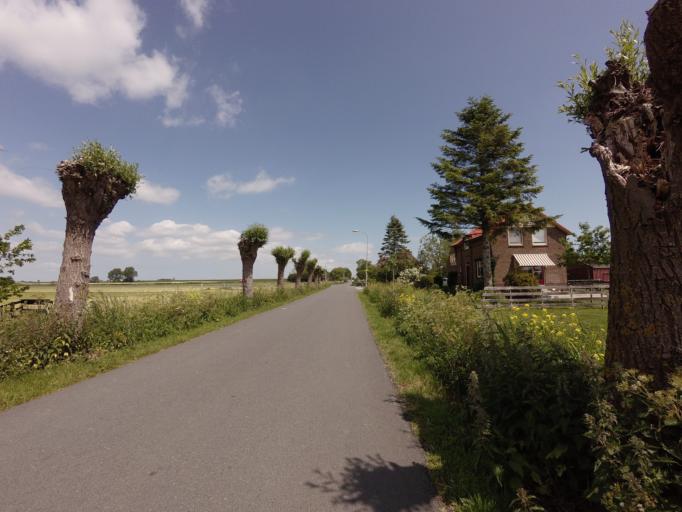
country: NL
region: North Holland
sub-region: Gemeente Hoorn
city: Hoorn
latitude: 52.5829
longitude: 5.0175
